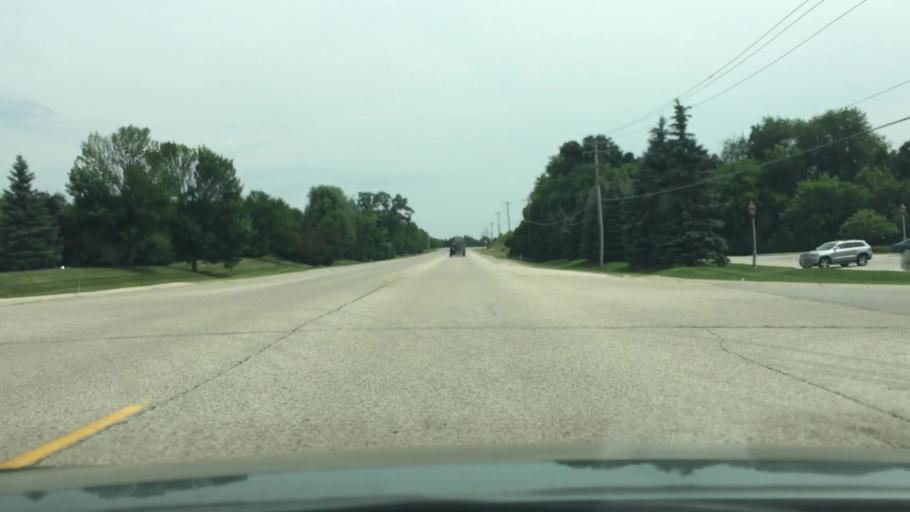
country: US
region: Wisconsin
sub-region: Waukesha County
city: Hartland
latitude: 43.0781
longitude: -88.3550
